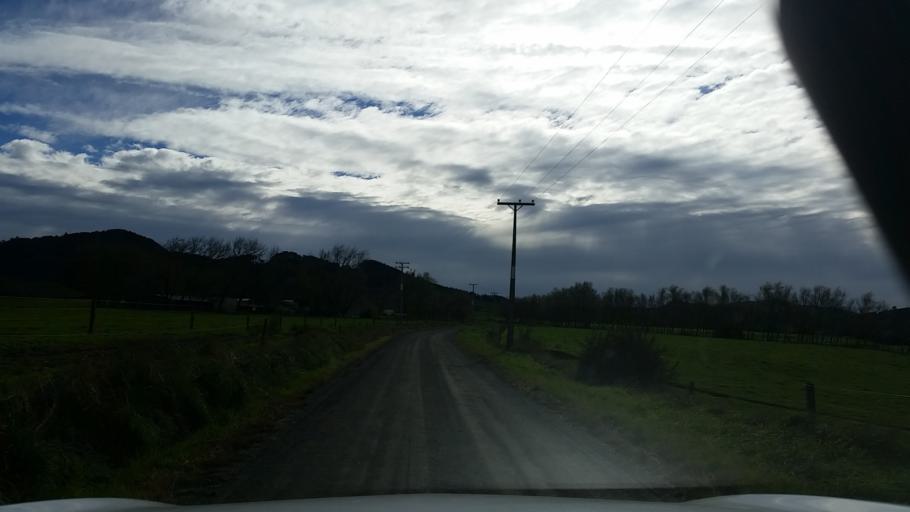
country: NZ
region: Waikato
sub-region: Hauraki District
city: Ngatea
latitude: -37.5065
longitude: 175.4068
